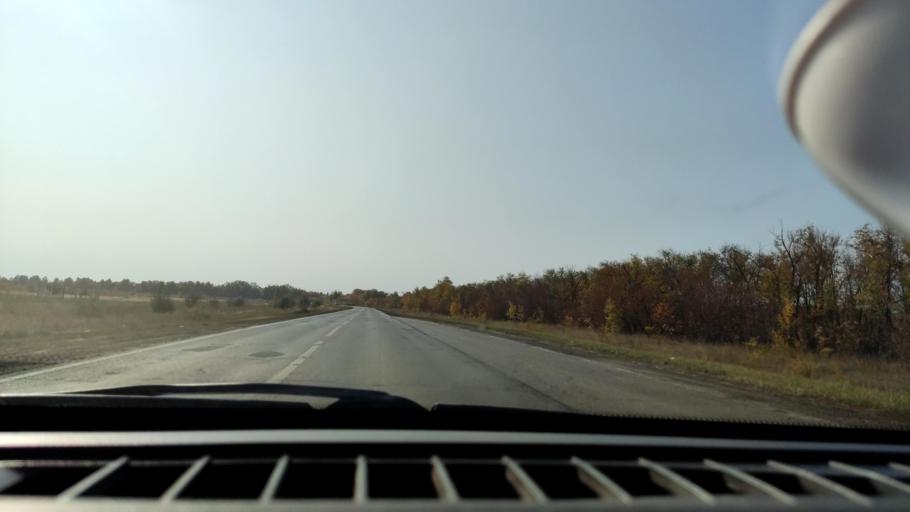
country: RU
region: Samara
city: Smyshlyayevka
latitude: 53.1395
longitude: 50.3806
